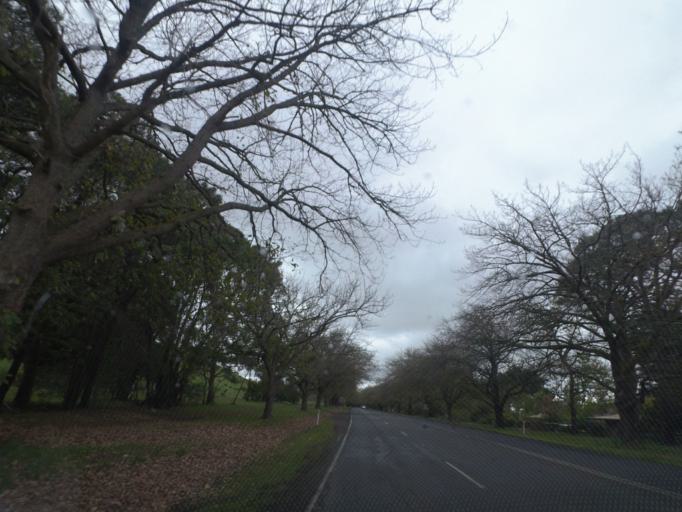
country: AU
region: Victoria
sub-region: Hume
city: Sunbury
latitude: -37.3467
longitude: 144.5349
